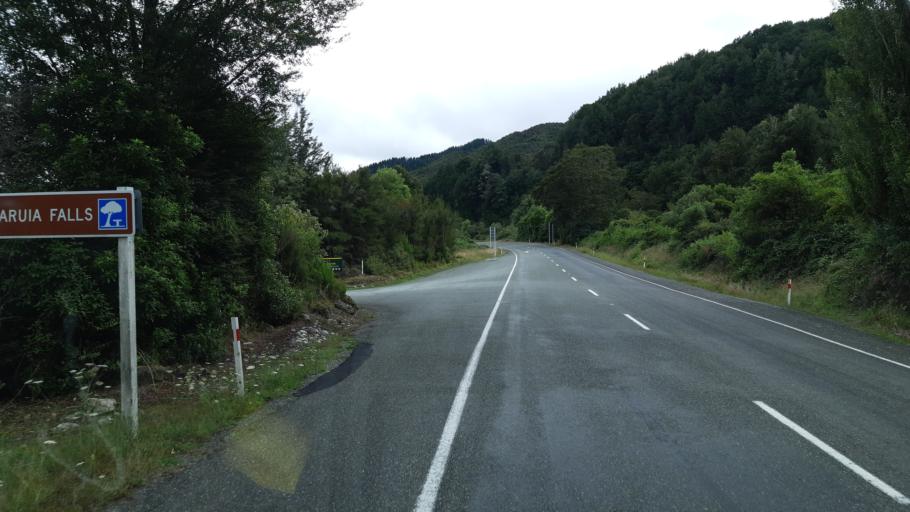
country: NZ
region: West Coast
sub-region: Buller District
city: Westport
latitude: -41.8597
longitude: 172.2532
